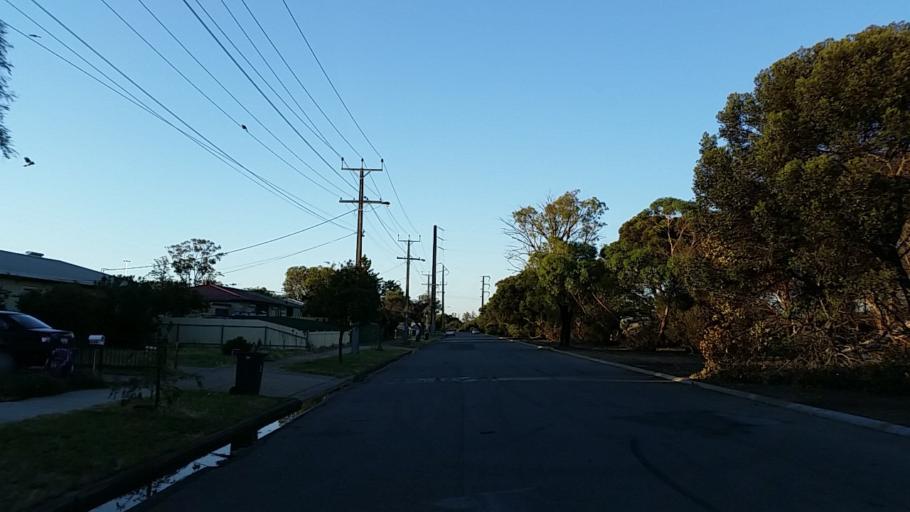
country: AU
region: South Australia
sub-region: Port Adelaide Enfield
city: Birkenhead
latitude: -34.8074
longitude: 138.5065
